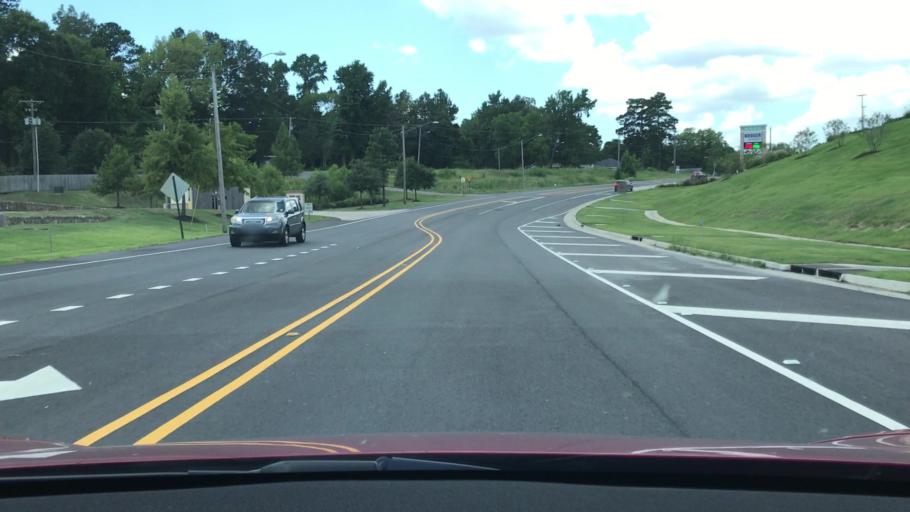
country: US
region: Louisiana
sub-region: Bossier Parish
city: Bossier City
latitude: 32.3942
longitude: -93.7258
